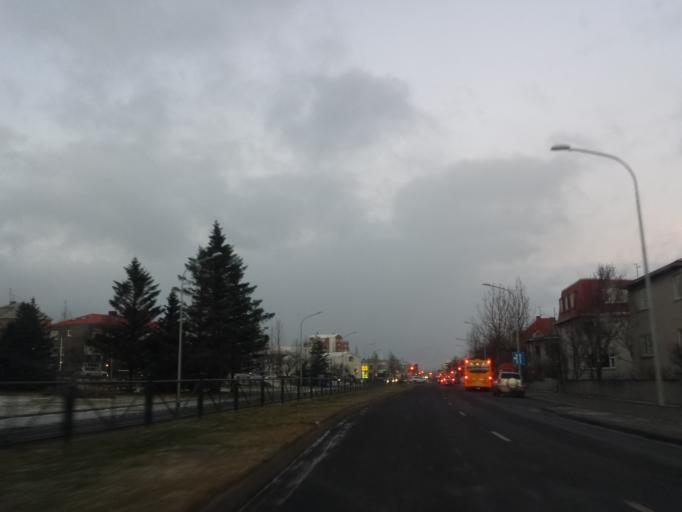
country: IS
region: Capital Region
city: Reykjavik
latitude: 64.1379
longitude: -21.9220
